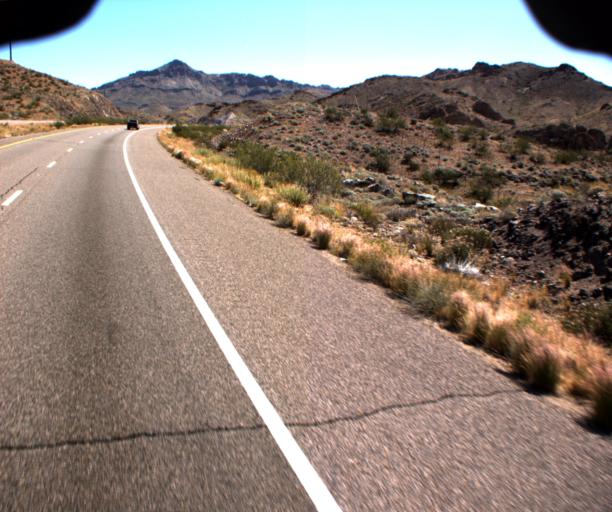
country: US
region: Nevada
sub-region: Clark County
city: Laughlin
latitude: 35.1945
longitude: -114.4384
